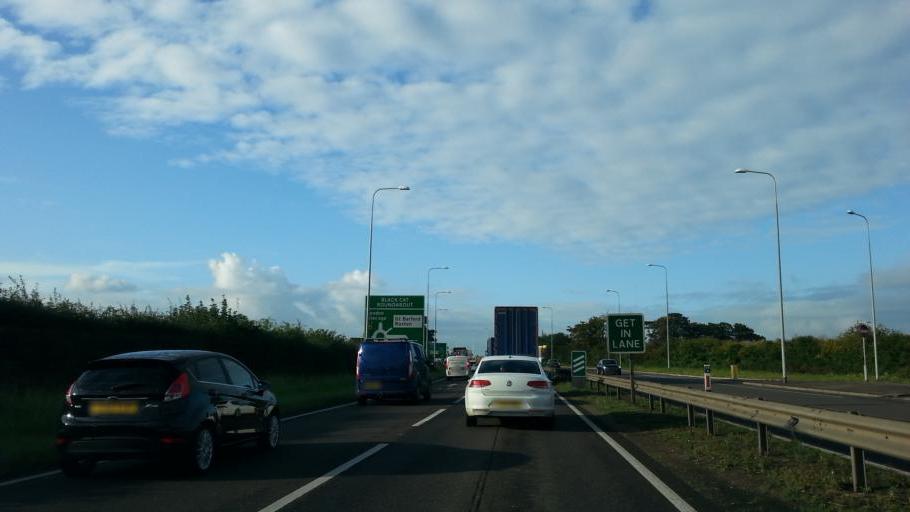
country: GB
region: England
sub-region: Bedford
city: Roxton
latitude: 52.1874
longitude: -0.3027
